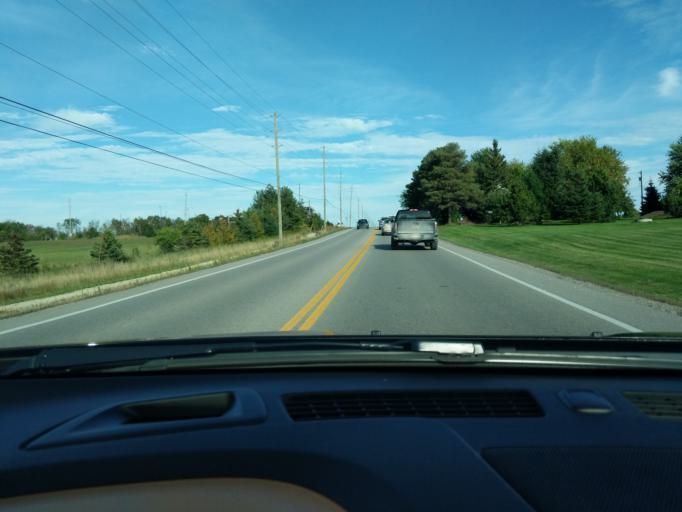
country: CA
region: Ontario
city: Collingwood
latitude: 44.4827
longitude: -80.1949
